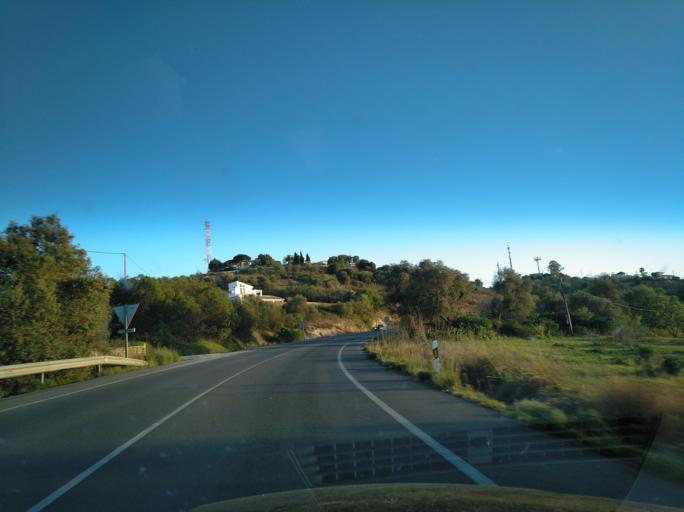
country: ES
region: Andalusia
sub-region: Provincia de Huelva
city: Ayamonte
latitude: 37.2303
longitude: -7.4010
